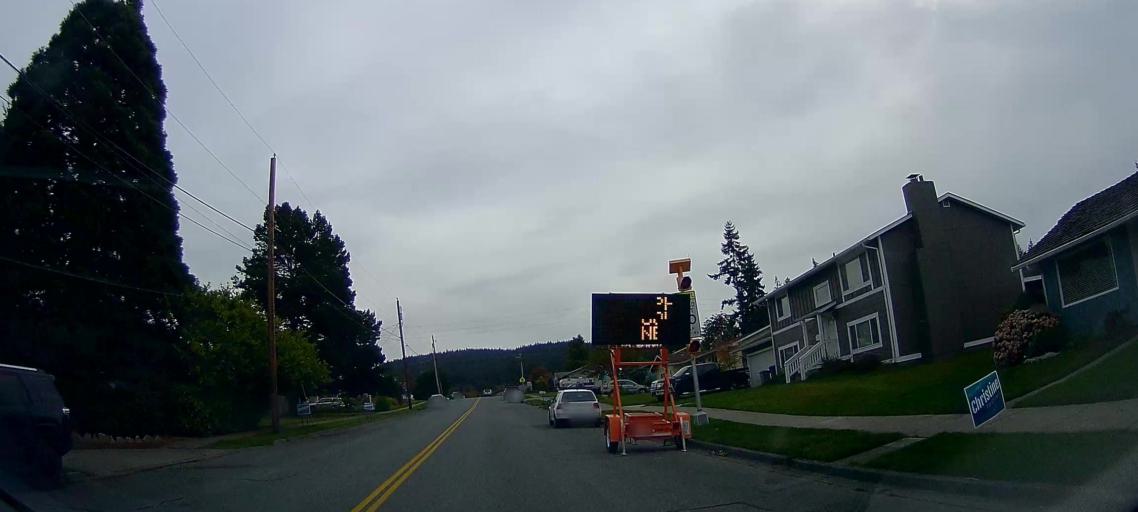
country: US
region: Washington
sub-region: Skagit County
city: Anacortes
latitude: 48.4896
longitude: -122.6180
